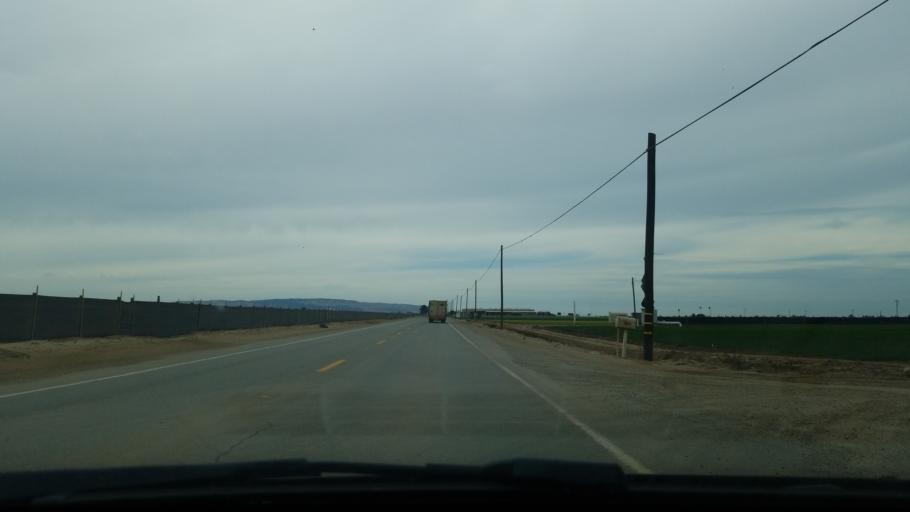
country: US
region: California
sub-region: Santa Barbara County
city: Santa Maria
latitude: 34.9236
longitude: -120.3858
